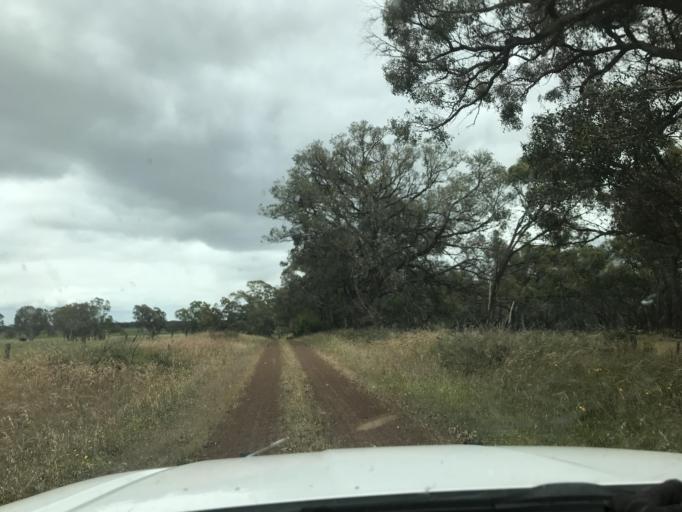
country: AU
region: South Australia
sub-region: Wattle Range
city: Penola
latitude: -37.0982
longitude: 141.2708
